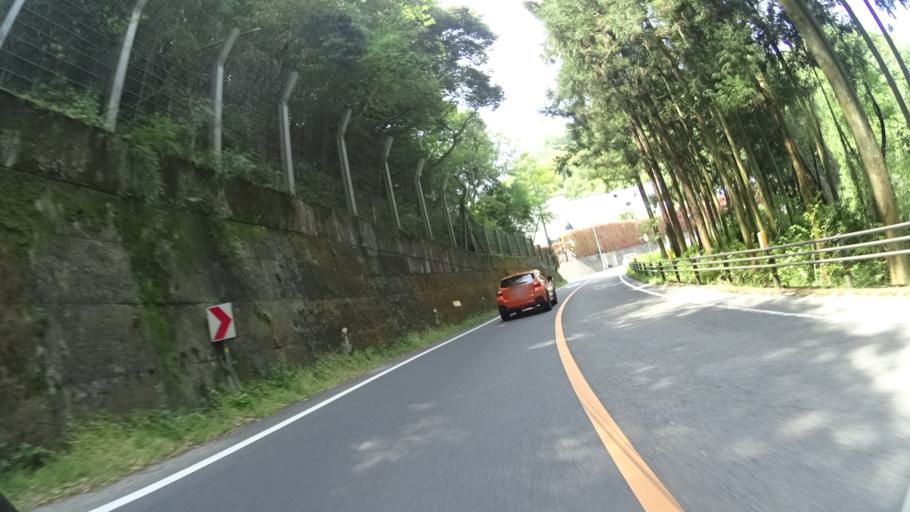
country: JP
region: Ehime
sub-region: Shikoku-chuo Shi
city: Matsuyama
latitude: 33.8849
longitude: 132.8352
